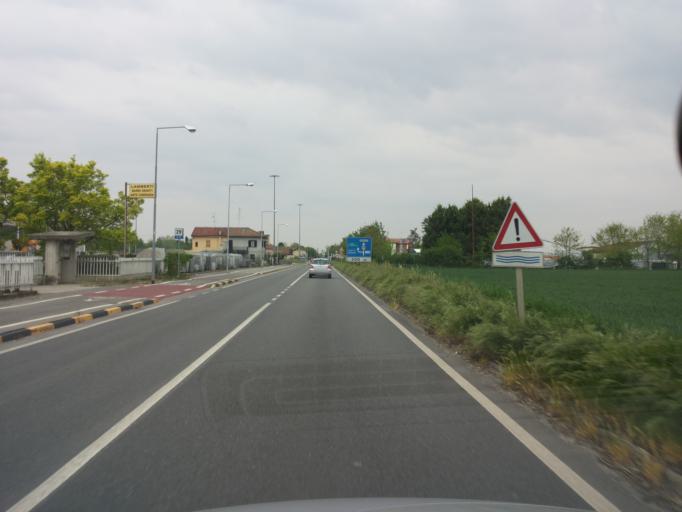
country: IT
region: Piedmont
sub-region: Provincia di Alessandria
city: Casale Monferrato
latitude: 45.1130
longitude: 8.4516
